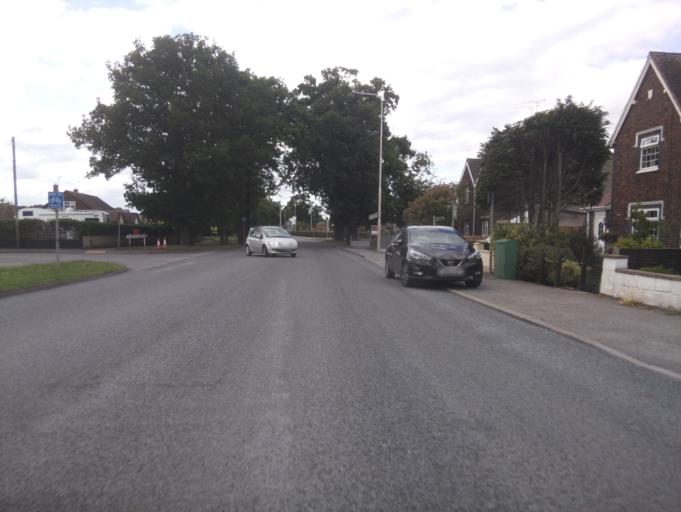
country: GB
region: England
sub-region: Warwickshire
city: Nuneaton
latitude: 52.5392
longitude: -1.4662
